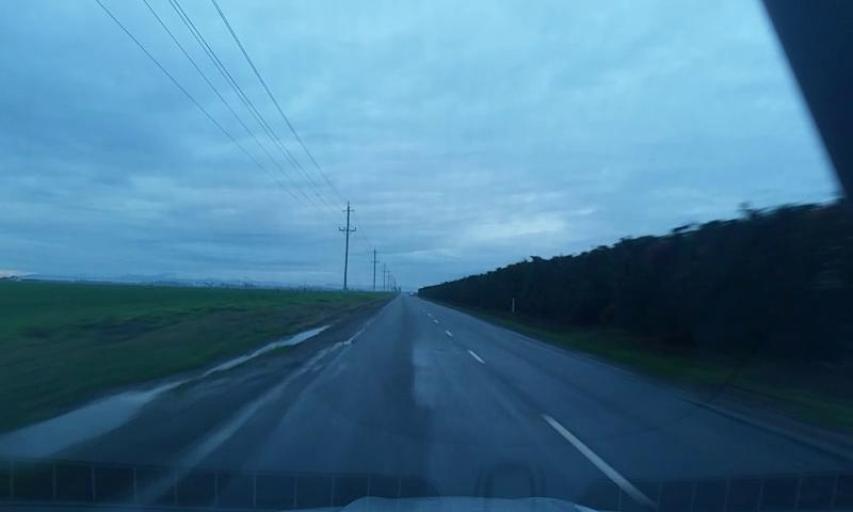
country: NZ
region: Canterbury
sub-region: Ashburton District
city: Rakaia
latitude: -43.7561
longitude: 171.9285
